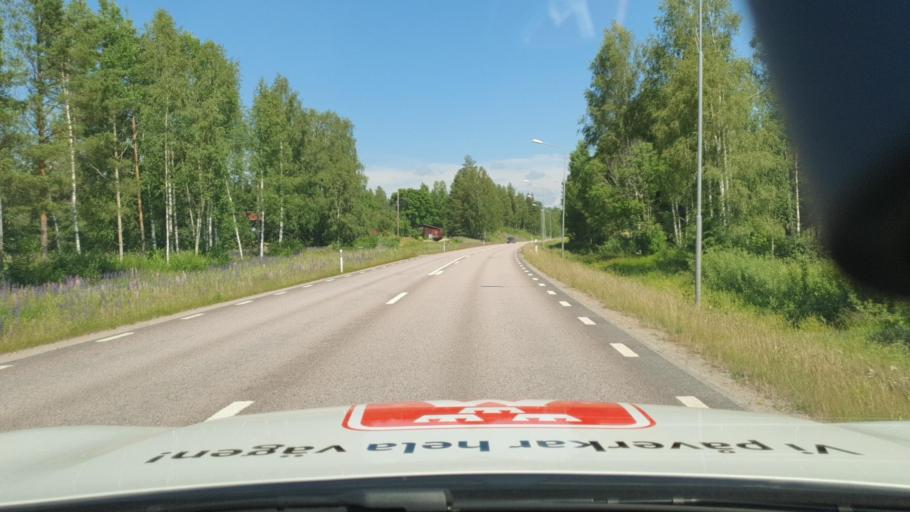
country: SE
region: Vaermland
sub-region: Torsby Kommun
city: Torsby
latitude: 60.1752
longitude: 13.0065
